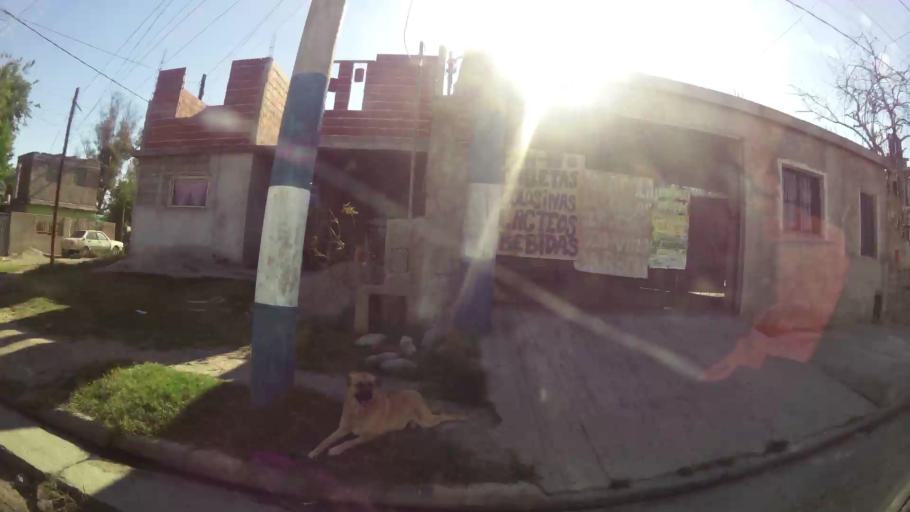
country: AR
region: Cordoba
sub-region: Departamento de Capital
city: Cordoba
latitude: -31.4002
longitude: -64.1528
